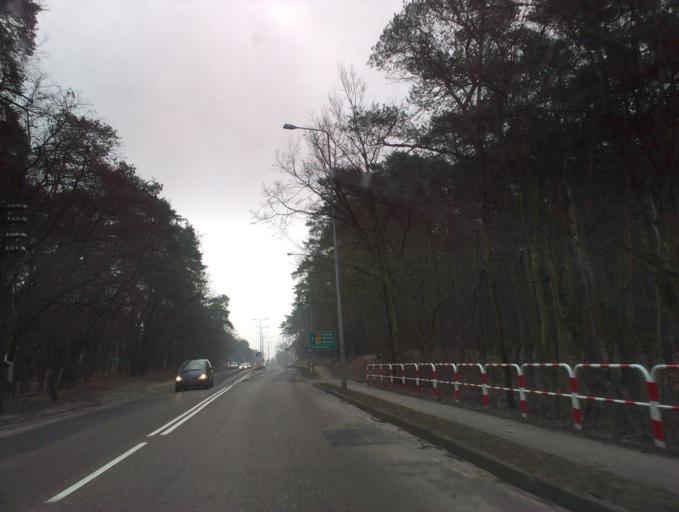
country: PL
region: Greater Poland Voivodeship
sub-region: Powiat chodzieski
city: Chodziez
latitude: 52.9891
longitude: 16.8956
